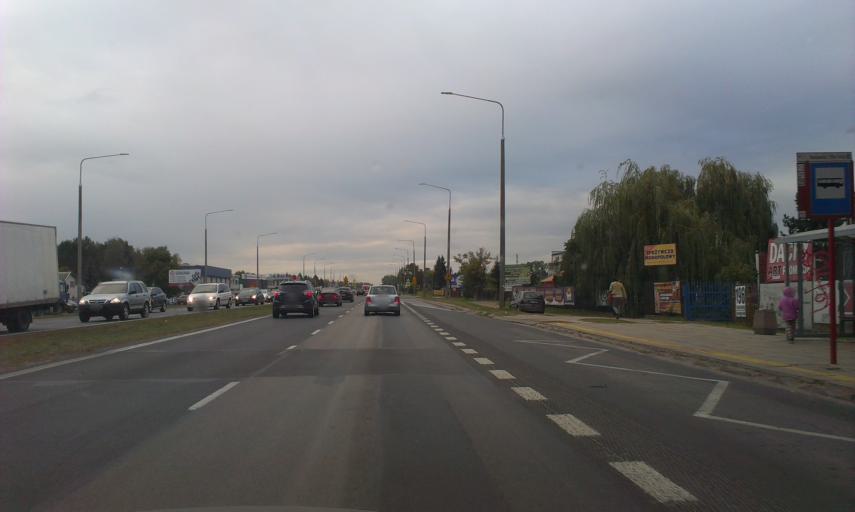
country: PL
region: Masovian Voivodeship
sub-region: Radom
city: Radom
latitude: 51.4433
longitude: 21.1453
